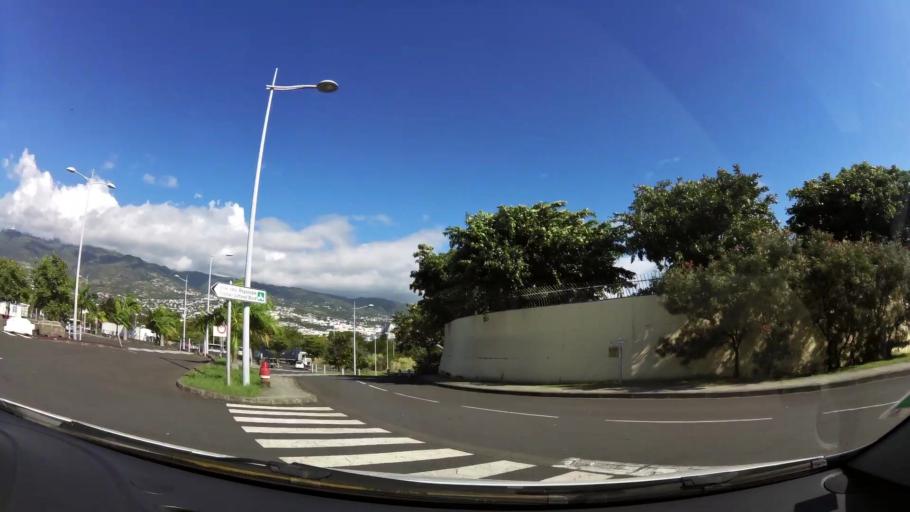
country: RE
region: Reunion
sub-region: Reunion
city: Sainte-Marie
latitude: -20.8958
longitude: 55.5023
